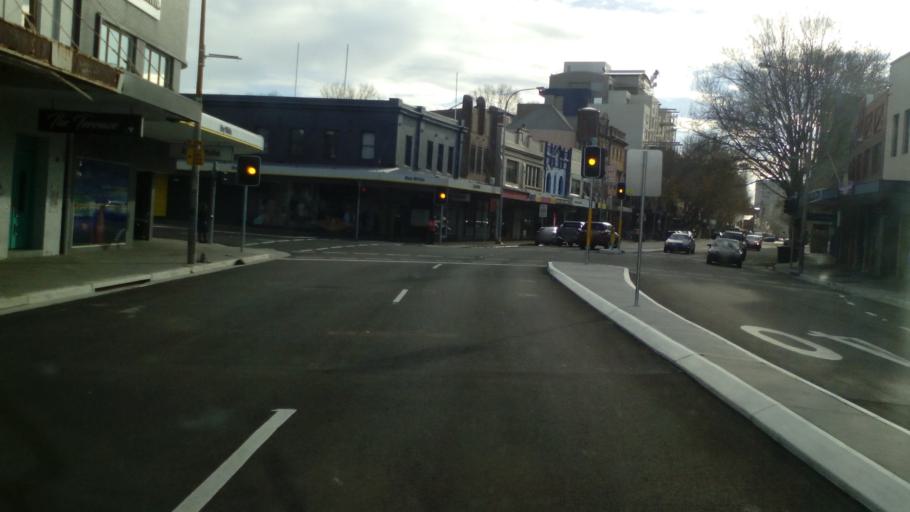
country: AU
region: New South Wales
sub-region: Newcastle
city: Cooks Hill
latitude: -32.9275
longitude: 151.7678
